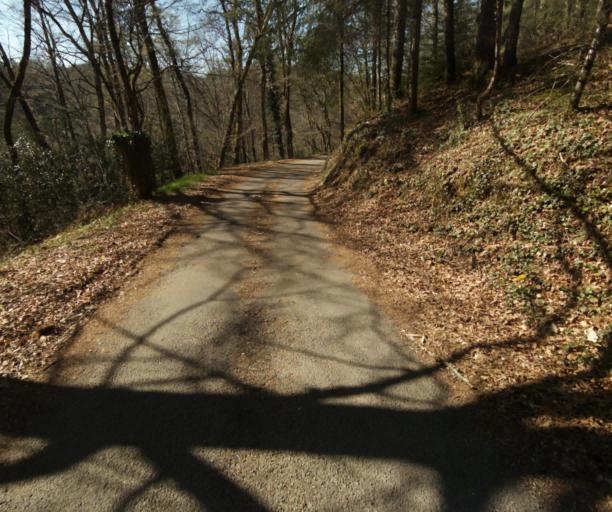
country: FR
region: Limousin
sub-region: Departement de la Correze
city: Tulle
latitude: 45.2775
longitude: 1.7360
